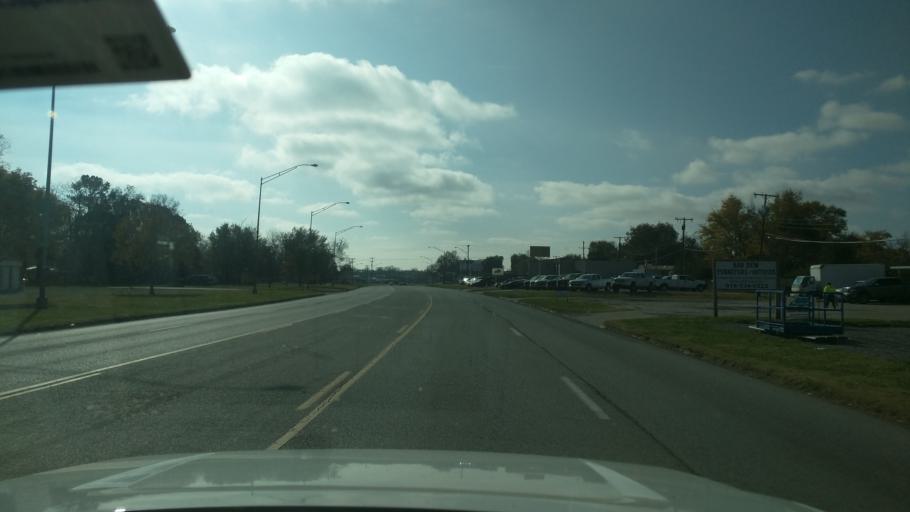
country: US
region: Oklahoma
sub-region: Washington County
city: Dewey
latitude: 36.7932
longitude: -95.9357
